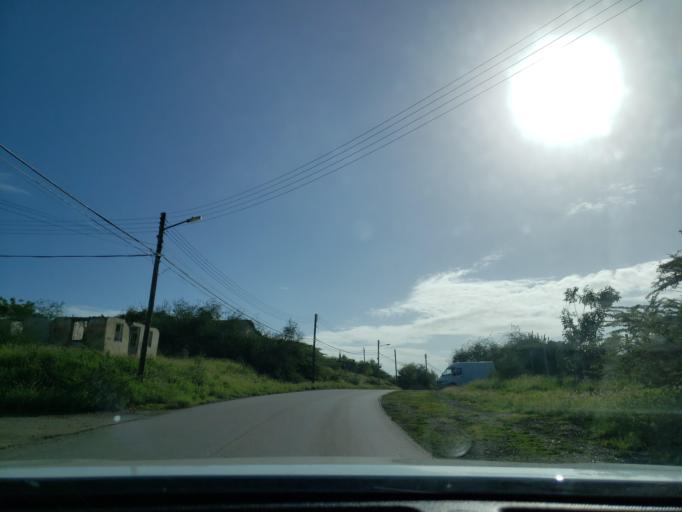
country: CW
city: Willemstad
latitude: 12.0937
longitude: -68.8714
